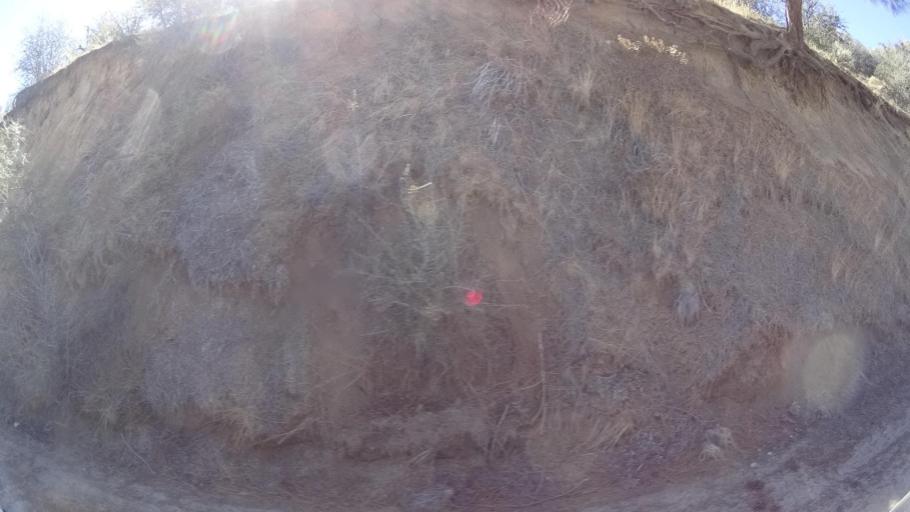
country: US
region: California
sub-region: Kern County
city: Alta Sierra
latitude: 35.7081
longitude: -118.5066
